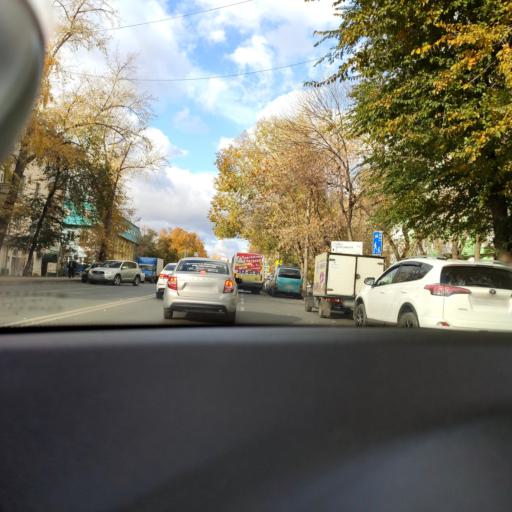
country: RU
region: Samara
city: Samara
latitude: 53.1900
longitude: 50.1311
